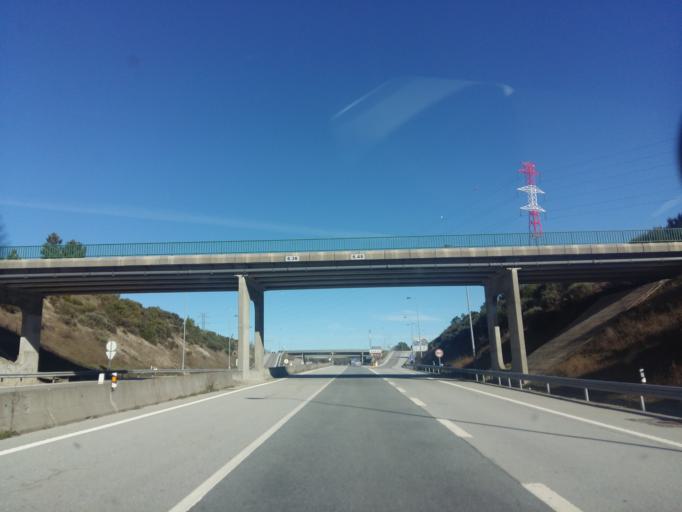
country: PT
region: Guarda
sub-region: Guarda
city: Sequeira
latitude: 40.5214
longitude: -7.2286
